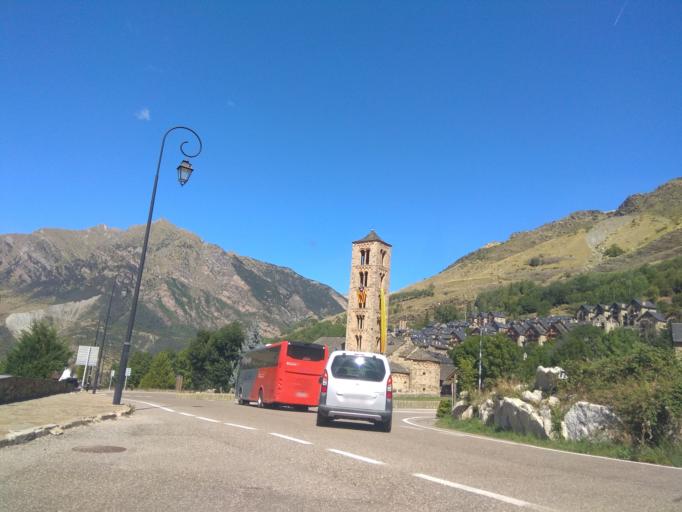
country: ES
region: Catalonia
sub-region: Provincia de Lleida
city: Vielha
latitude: 42.5171
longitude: 0.8487
